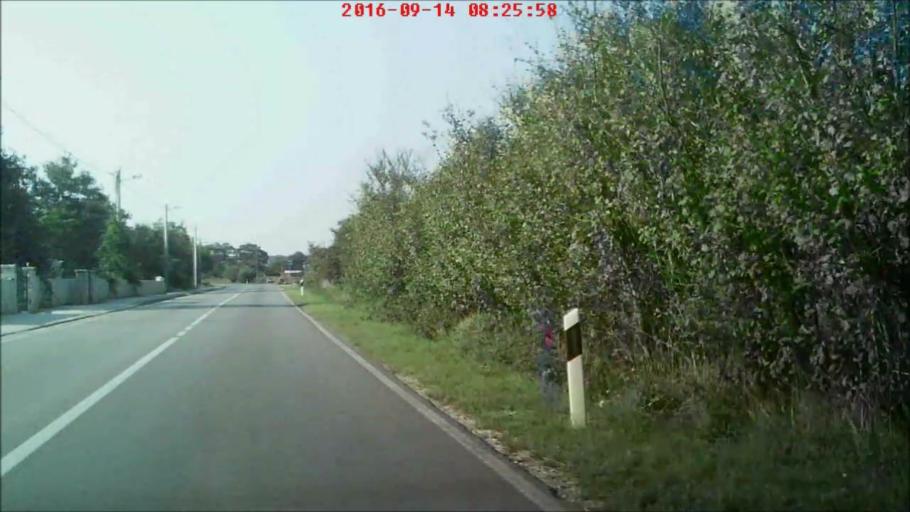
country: HR
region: Zadarska
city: Vrsi
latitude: 44.1996
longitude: 15.2572
